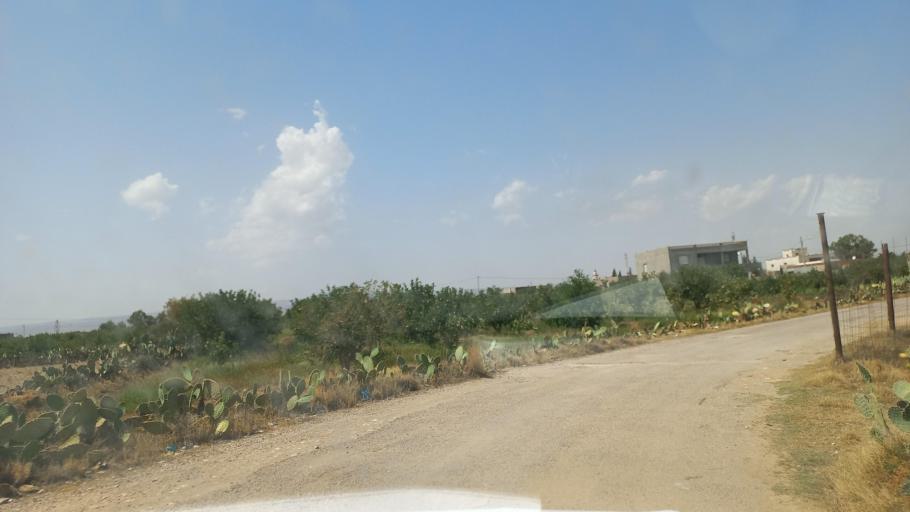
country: TN
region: Al Qasrayn
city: Kasserine
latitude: 35.2475
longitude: 9.0281
